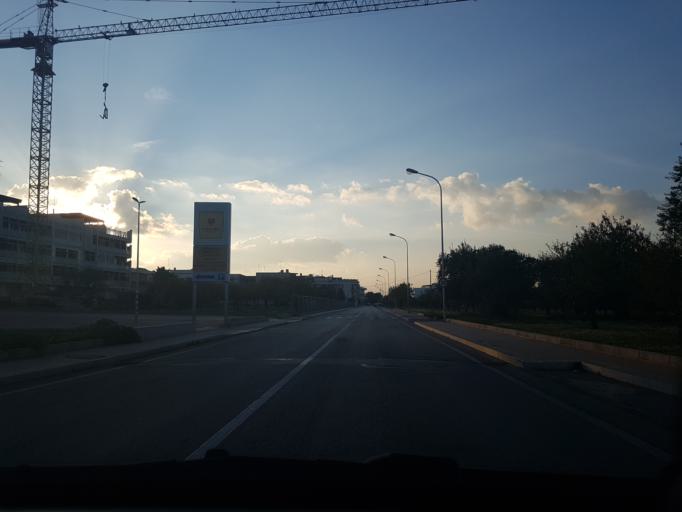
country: IT
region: Apulia
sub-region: Provincia di Bari
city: Bitritto
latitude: 41.0474
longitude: 16.8308
